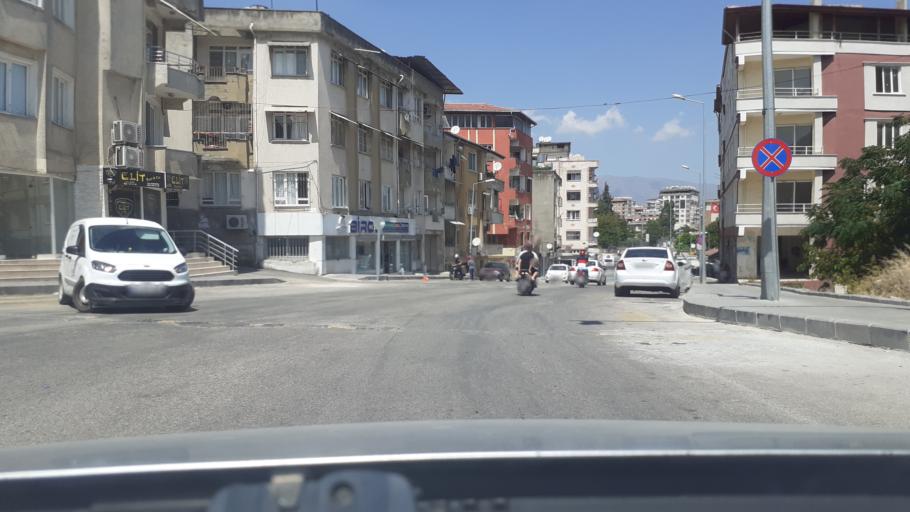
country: TR
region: Hatay
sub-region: Antakya Ilcesi
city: Antakya
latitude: 36.1980
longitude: 36.1545
